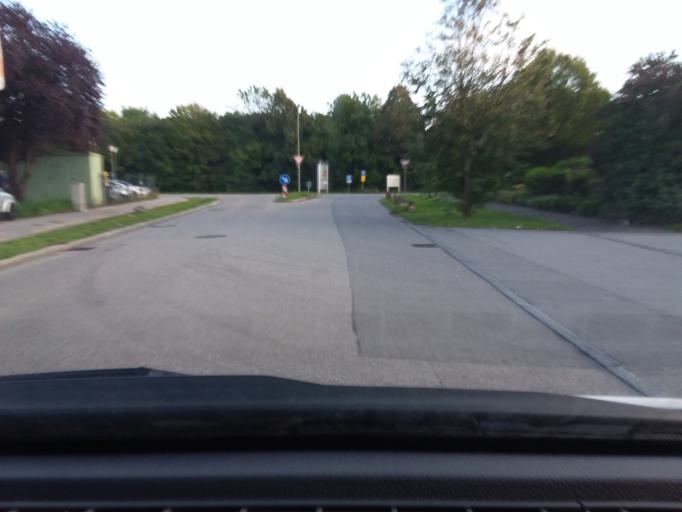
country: DE
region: Bavaria
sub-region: Upper Bavaria
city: Oberschleissheim
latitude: 48.2508
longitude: 11.6073
